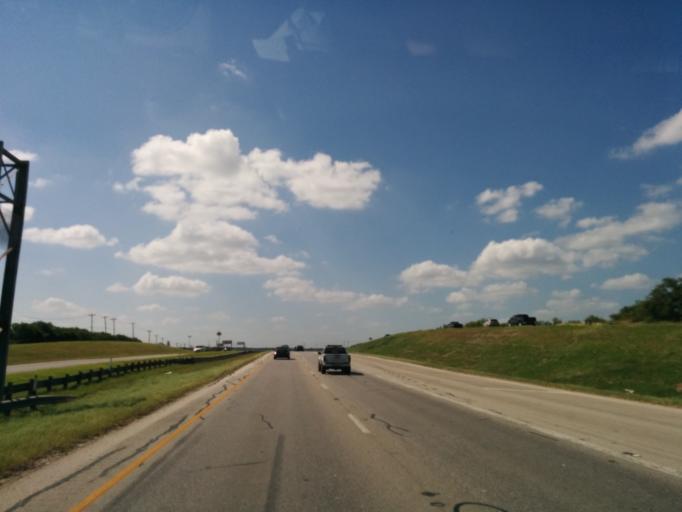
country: US
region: Texas
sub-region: Bexar County
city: Live Oak
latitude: 29.5852
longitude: -98.3473
